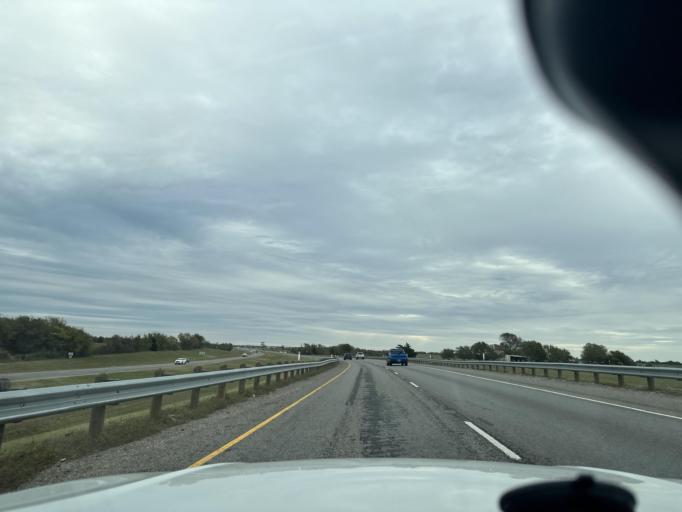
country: US
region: Texas
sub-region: Burleson County
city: Somerville
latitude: 30.1516
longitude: -96.6296
